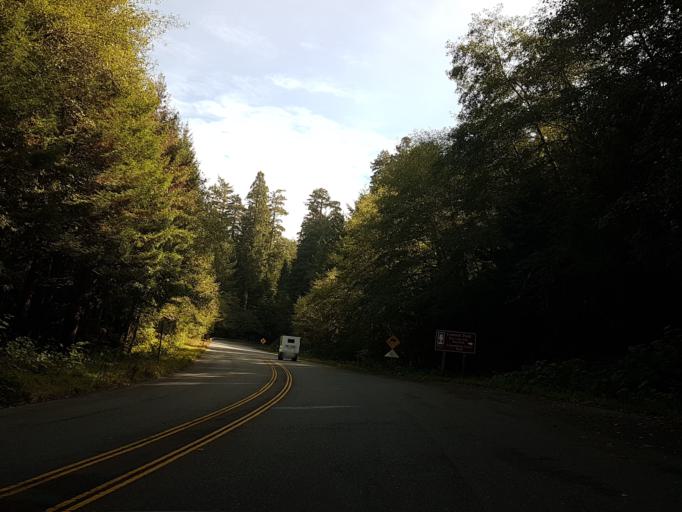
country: US
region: California
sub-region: Del Norte County
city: Bertsch-Oceanview
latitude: 41.4582
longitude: -124.0468
